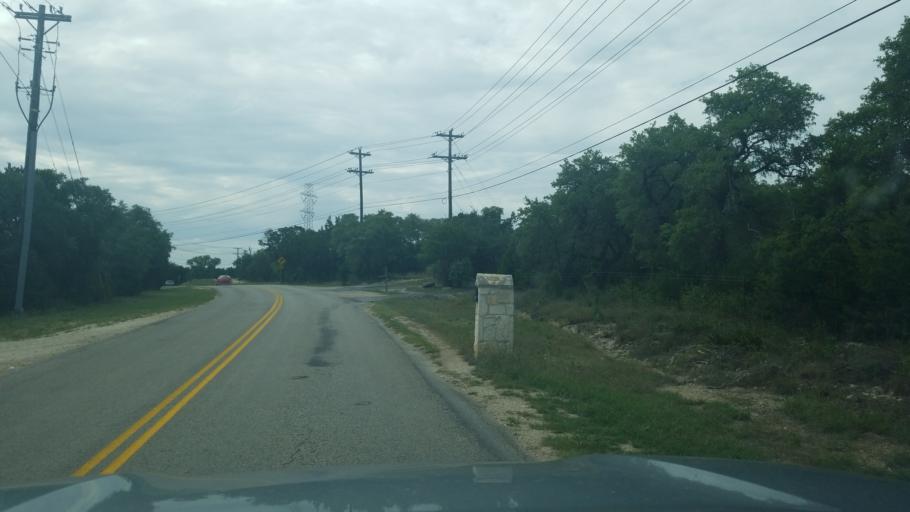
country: US
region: Texas
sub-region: Comal County
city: Bulverde
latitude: 29.7795
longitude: -98.4138
